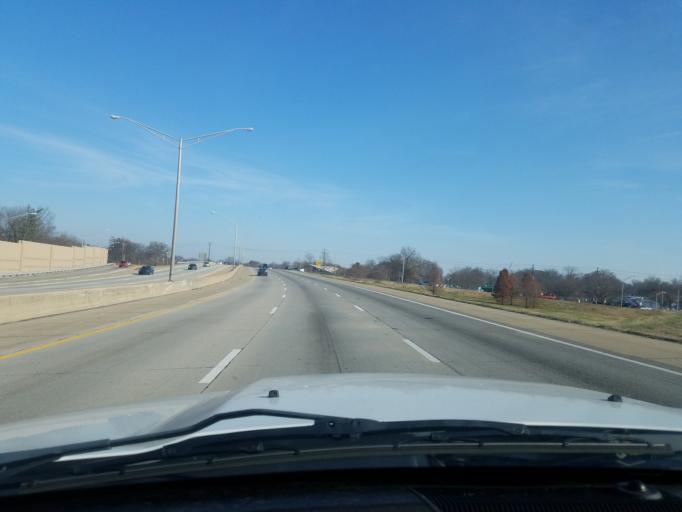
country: US
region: Kentucky
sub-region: Jefferson County
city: Shively
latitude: 38.1873
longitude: -85.7870
